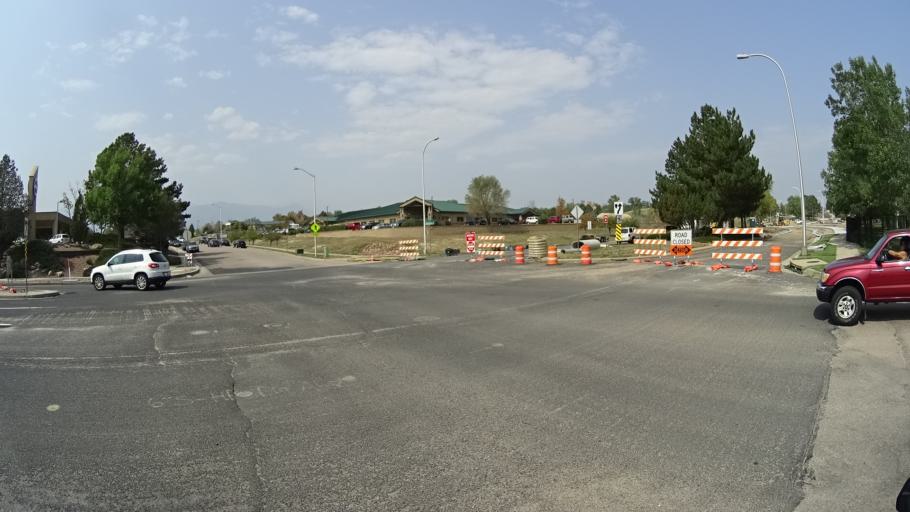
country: US
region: Colorado
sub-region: El Paso County
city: Colorado Springs
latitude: 38.8276
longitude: -104.7864
